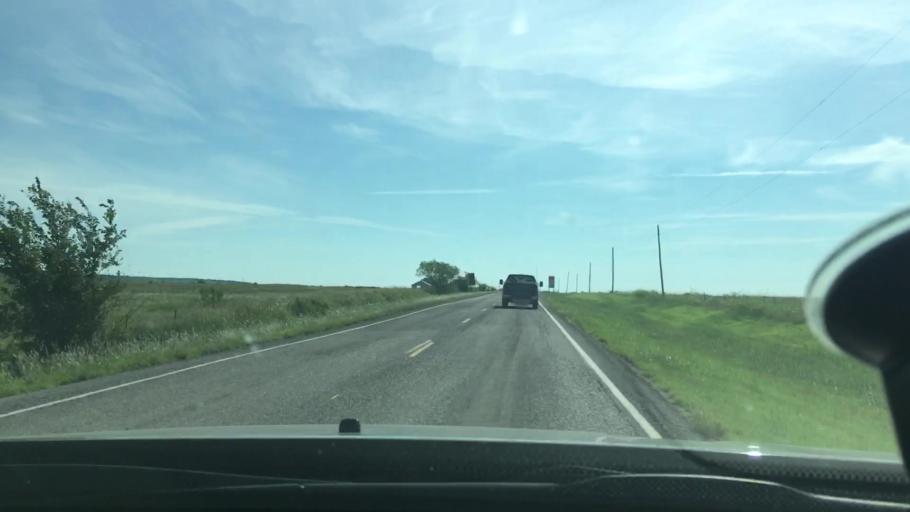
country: US
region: Oklahoma
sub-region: Carter County
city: Lone Grove
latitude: 34.3327
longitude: -97.2578
